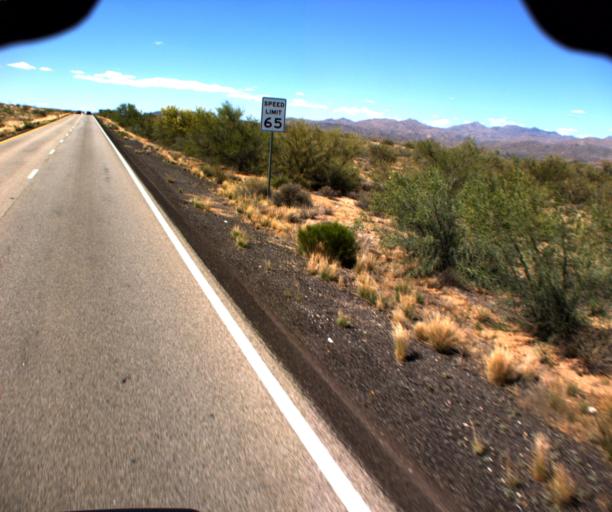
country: US
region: Arizona
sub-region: Mohave County
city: Kingman
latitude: 34.8706
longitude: -113.6445
